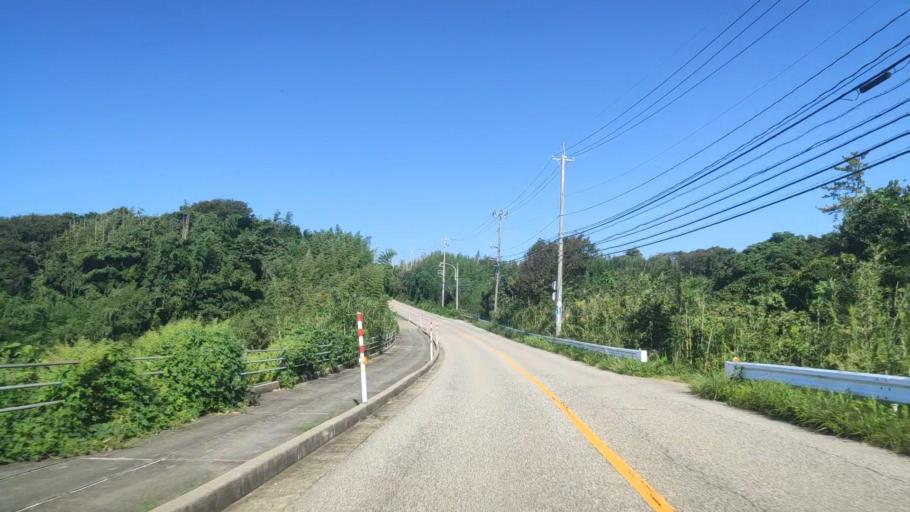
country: JP
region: Ishikawa
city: Hakui
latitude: 37.0509
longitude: 136.7350
